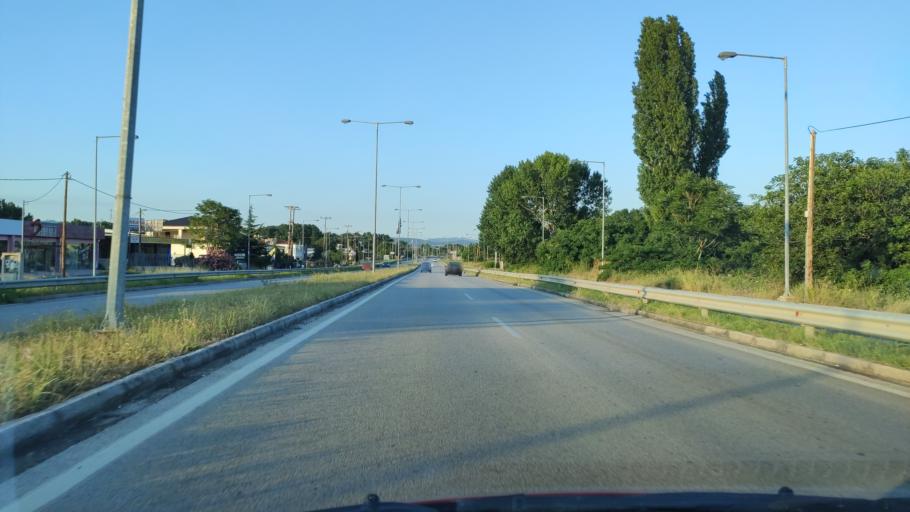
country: GR
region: East Macedonia and Thrace
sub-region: Nomos Rodopis
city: Komotini
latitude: 41.1113
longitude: 25.3722
